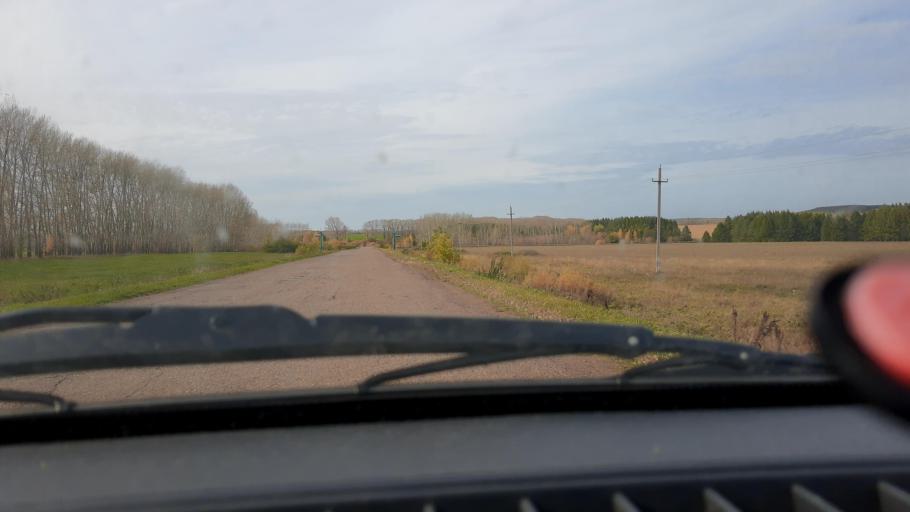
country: RU
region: Bashkortostan
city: Chekmagush
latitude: 54.8871
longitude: 54.5846
